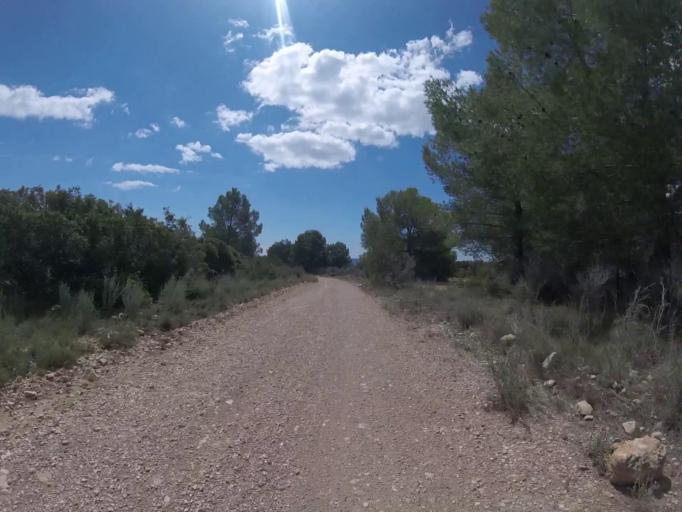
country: ES
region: Valencia
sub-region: Provincia de Castello
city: Alcoceber
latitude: 40.2851
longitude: 0.3233
